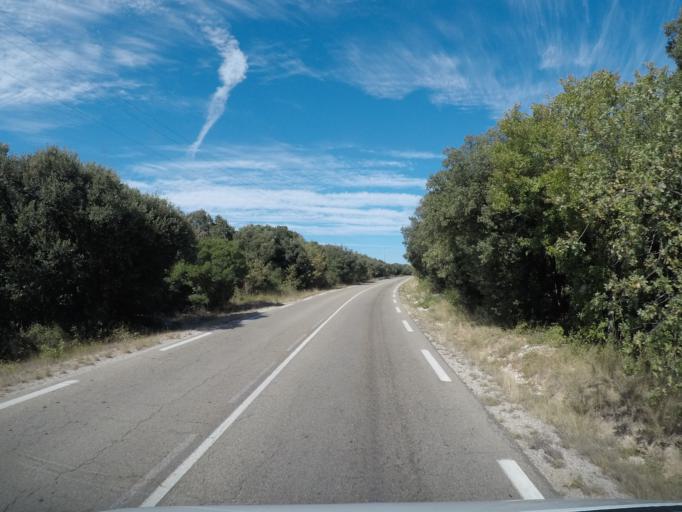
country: FR
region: Languedoc-Roussillon
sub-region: Departement de l'Herault
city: Saint-Martin-de-Londres
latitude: 43.7656
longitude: 3.7458
